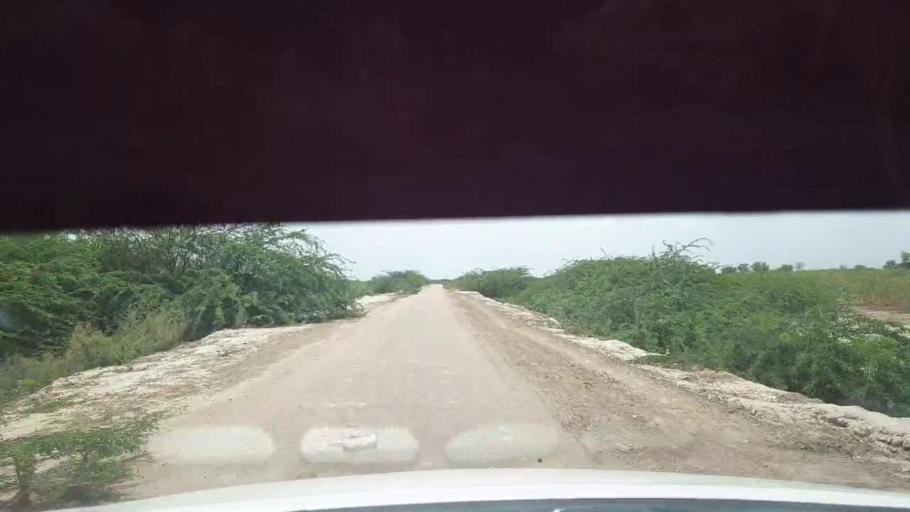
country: PK
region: Sindh
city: Kadhan
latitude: 24.5261
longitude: 69.0891
